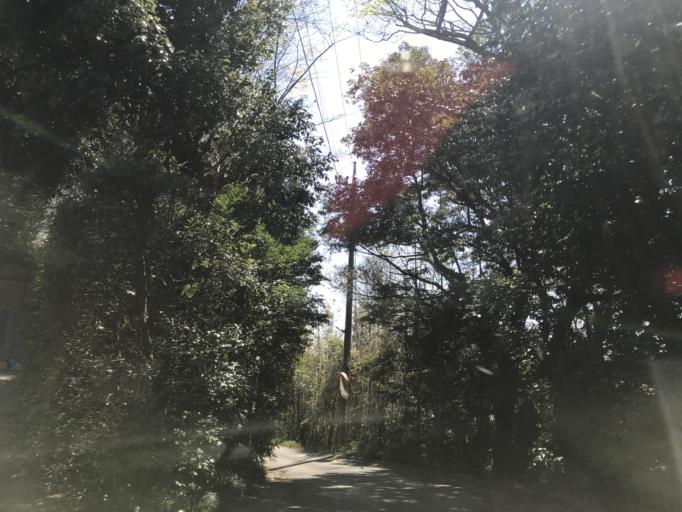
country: JP
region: Ibaraki
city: Moriya
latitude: 35.9364
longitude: 139.9755
